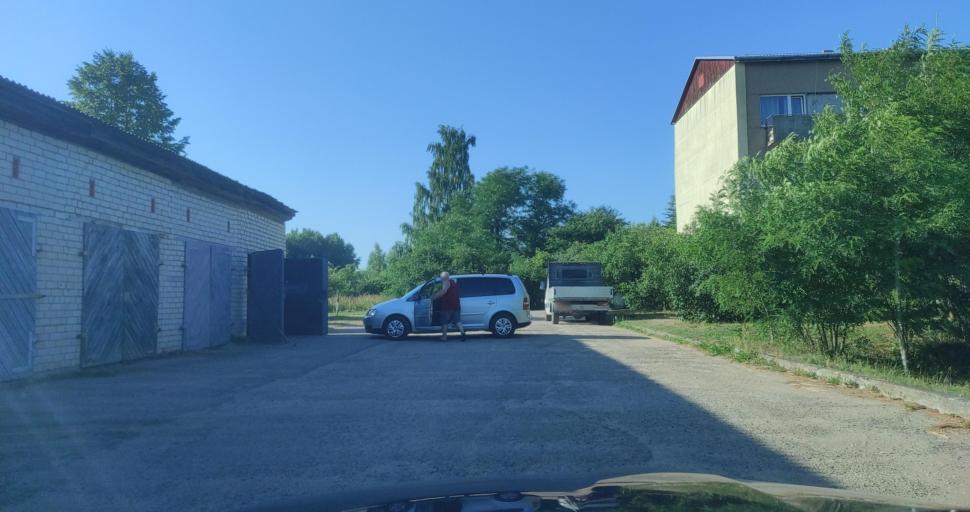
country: LV
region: Skrunda
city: Skrunda
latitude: 56.6719
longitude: 21.9996
